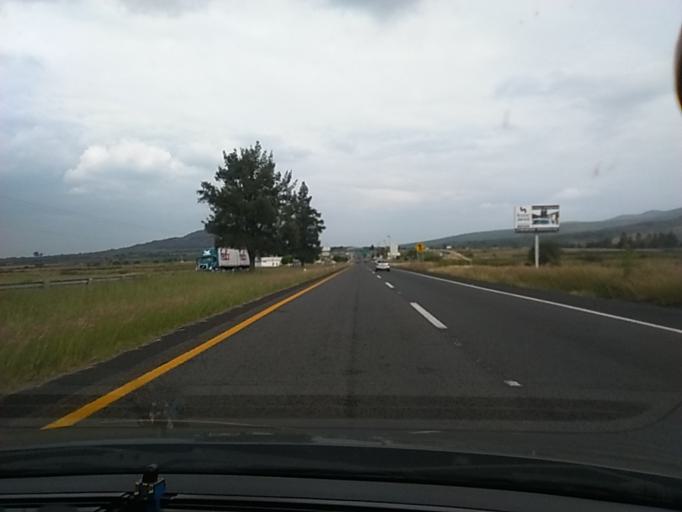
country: MX
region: Michoacan
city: Ecuandureo
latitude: 20.1752
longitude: -102.1955
